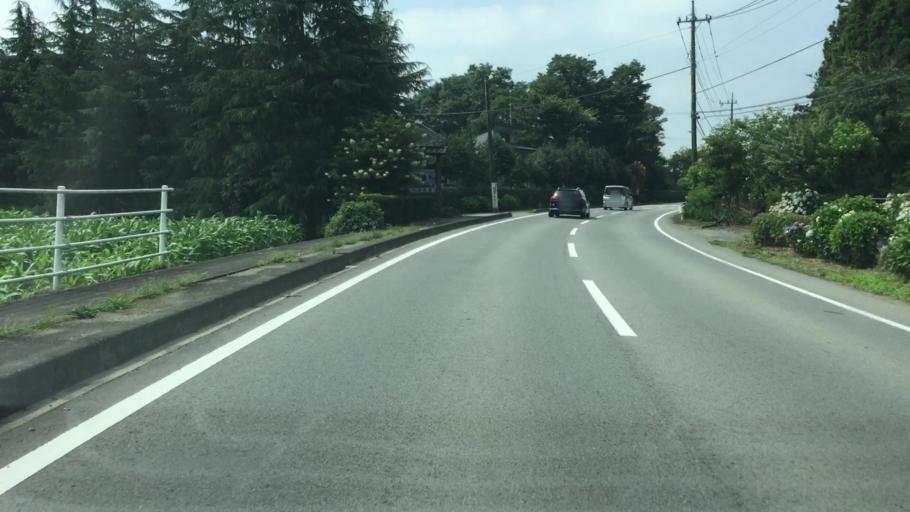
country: JP
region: Tochigi
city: Kuroiso
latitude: 36.9972
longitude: 139.9956
